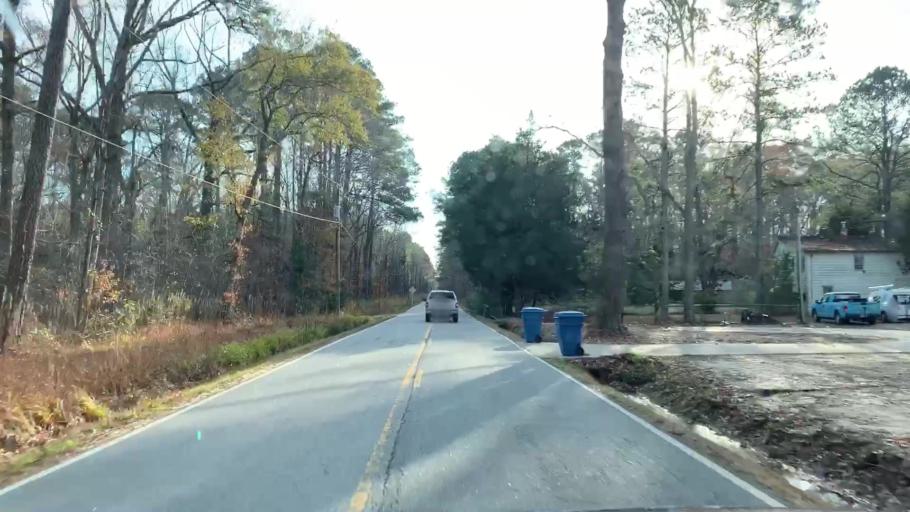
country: US
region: Virginia
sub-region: City of Virginia Beach
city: Virginia Beach
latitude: 36.7412
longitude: -76.1126
